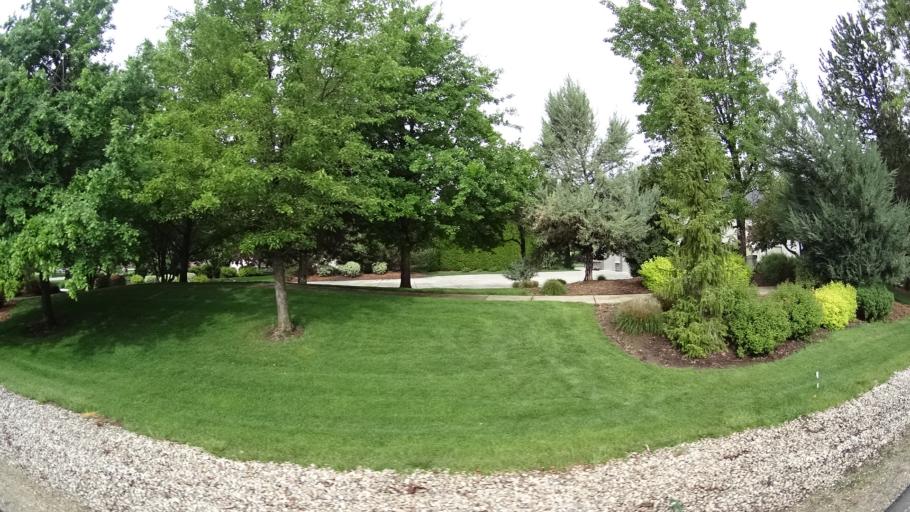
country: US
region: Idaho
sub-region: Ada County
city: Eagle
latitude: 43.7170
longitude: -116.3792
